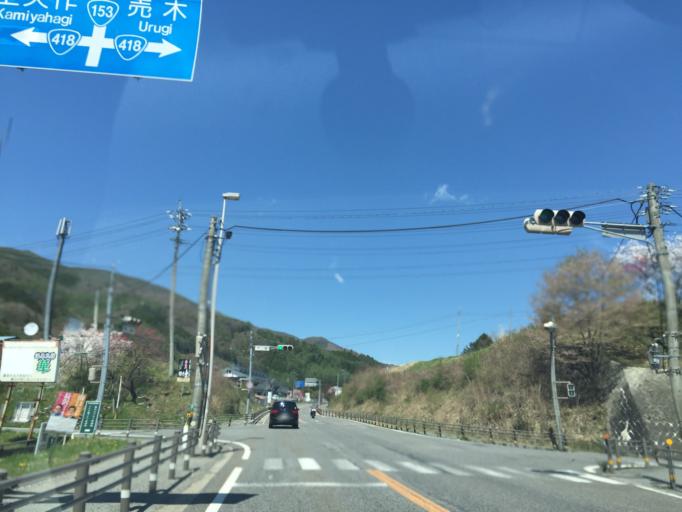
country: JP
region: Gifu
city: Nakatsugawa
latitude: 35.3209
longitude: 137.6287
